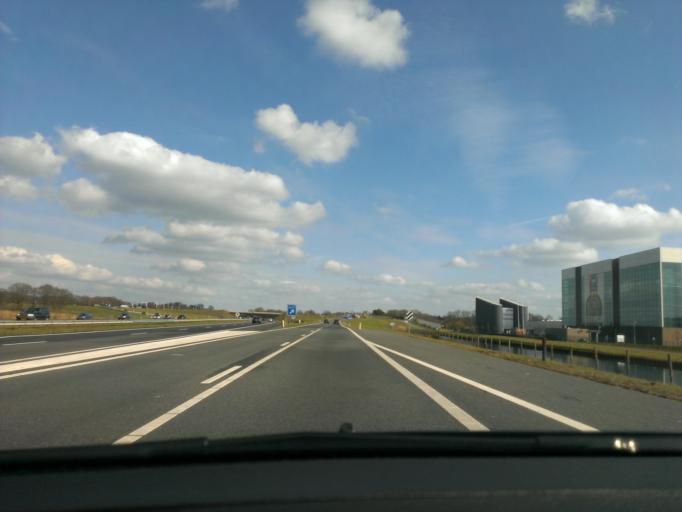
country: NL
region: Overijssel
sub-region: Gemeente Hengelo
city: Hengelo
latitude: 52.2091
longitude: 6.8156
